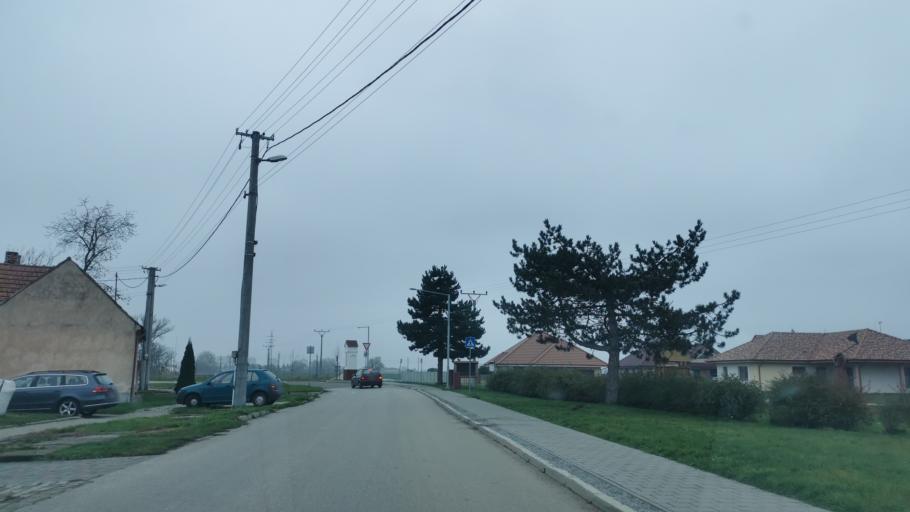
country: SK
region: Trnavsky
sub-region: Okres Skalica
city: Holic
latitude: 48.8312
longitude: 17.1687
